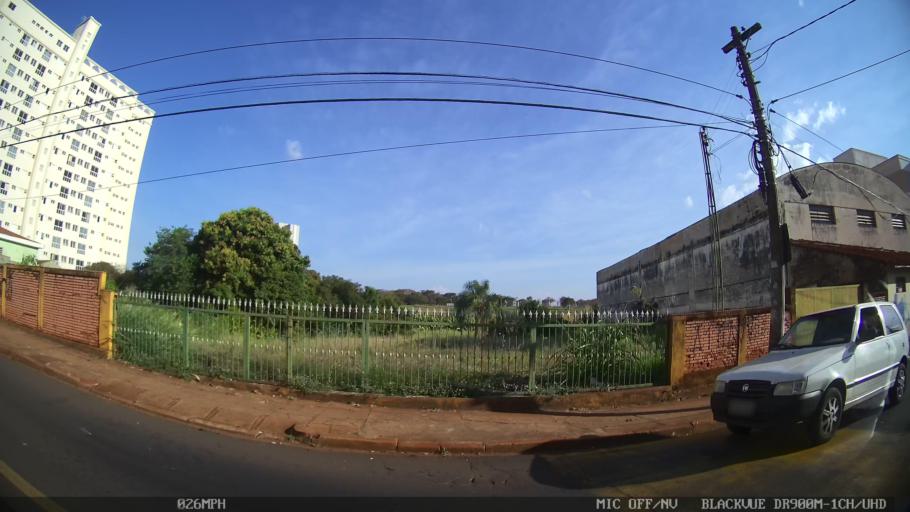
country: BR
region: Sao Paulo
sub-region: Ribeirao Preto
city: Ribeirao Preto
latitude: -21.1907
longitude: -47.7893
